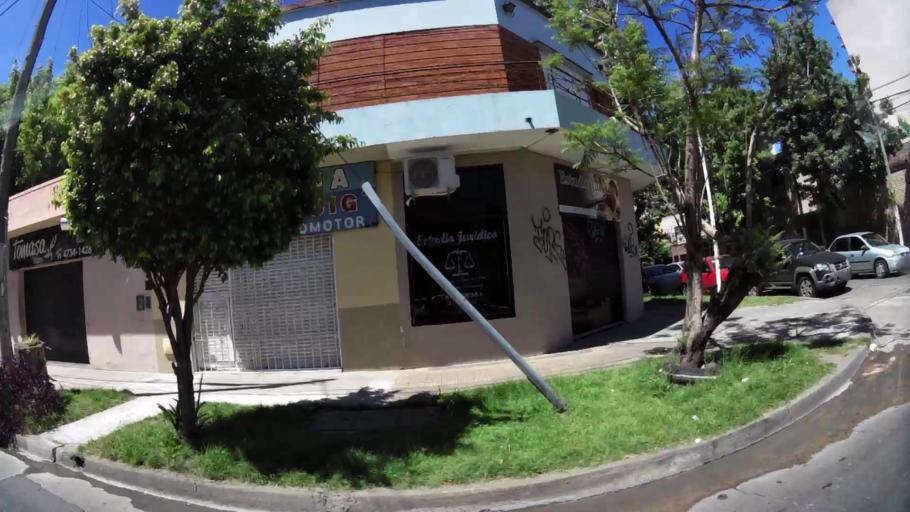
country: AR
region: Buenos Aires
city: Caseros
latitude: -34.6014
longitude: -58.5602
